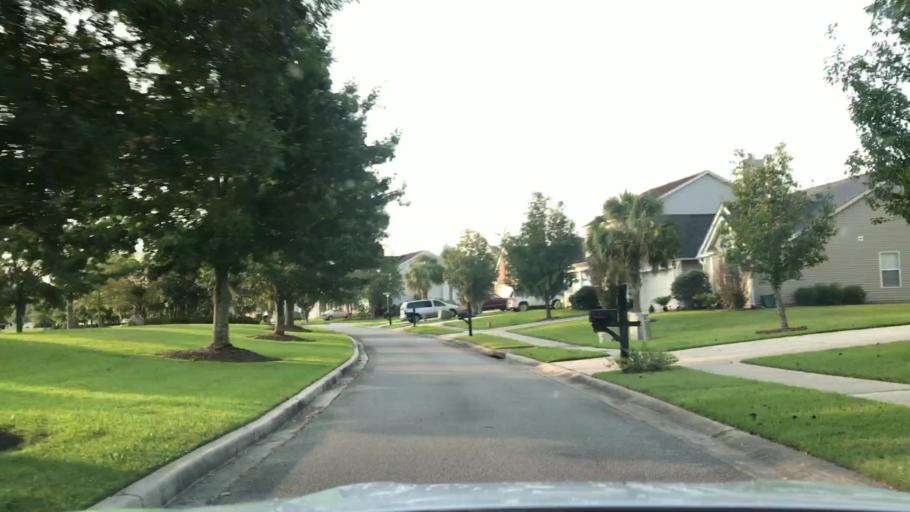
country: US
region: South Carolina
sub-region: Charleston County
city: Shell Point
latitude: 32.8361
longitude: -80.0927
